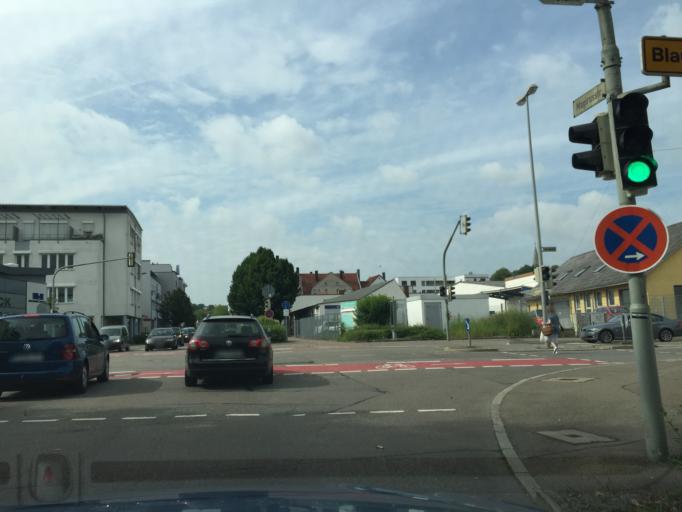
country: DE
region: Baden-Wuerttemberg
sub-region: Tuebingen Region
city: Ulm
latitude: 48.3963
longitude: 9.9644
